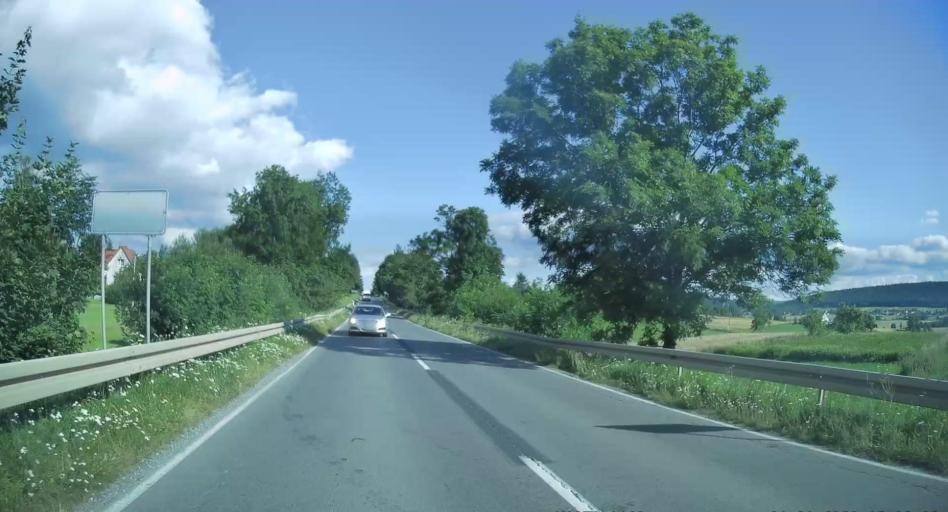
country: PL
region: Swietokrzyskie
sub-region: Powiat kielecki
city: Bodzentyn
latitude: 50.9686
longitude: 20.8864
